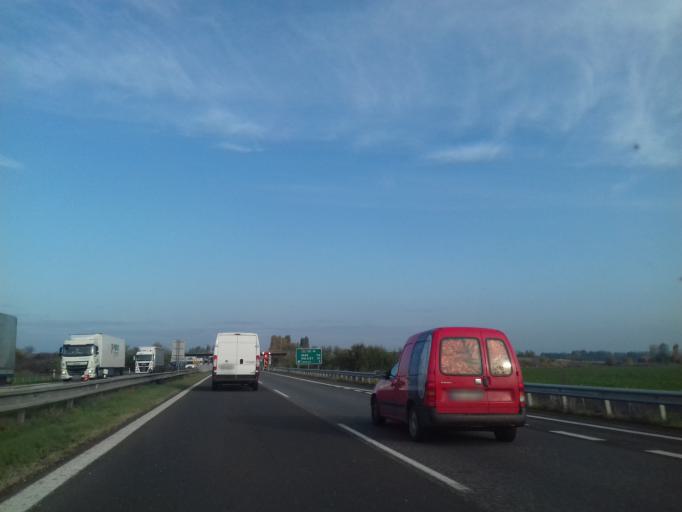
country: SK
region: Bratislavsky
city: Stupava
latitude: 48.2542
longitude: 17.0114
